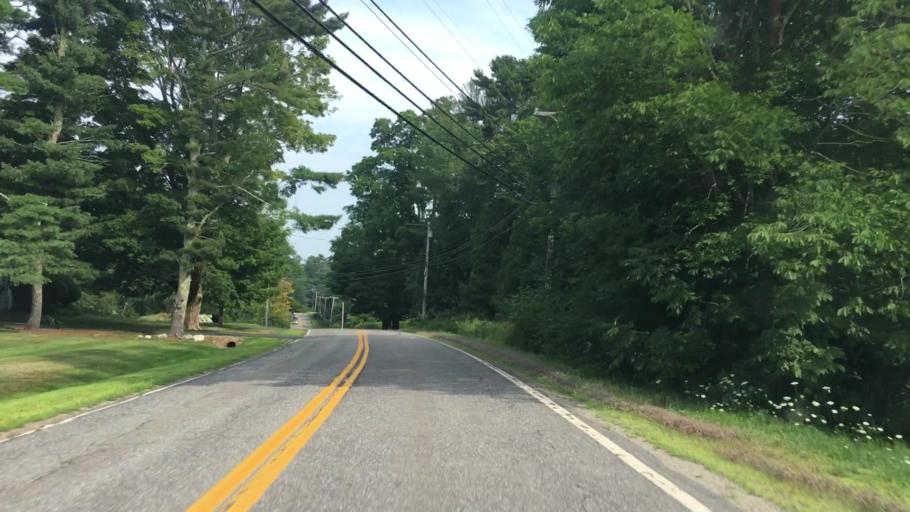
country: US
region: Maine
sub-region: Lincoln County
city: Waldoboro
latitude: 44.0704
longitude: -69.3616
